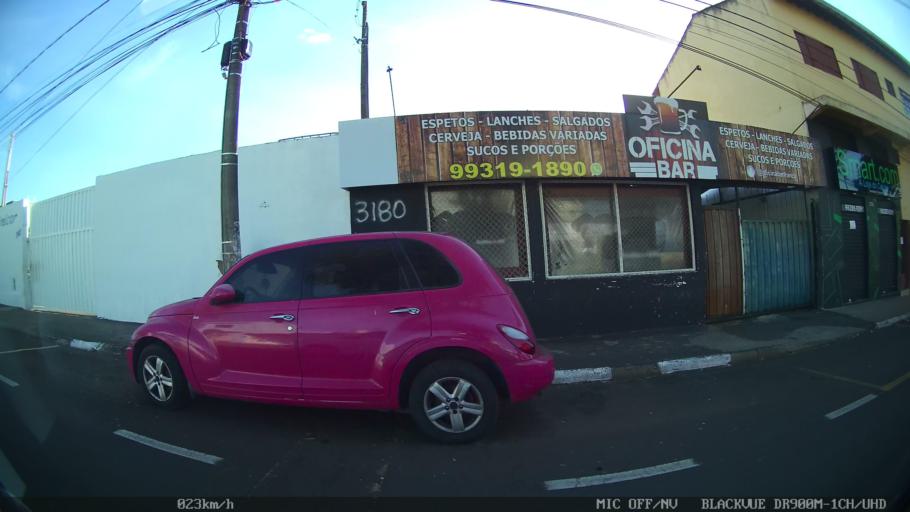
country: BR
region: Sao Paulo
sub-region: Franca
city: Franca
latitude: -20.5431
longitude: -47.3873
